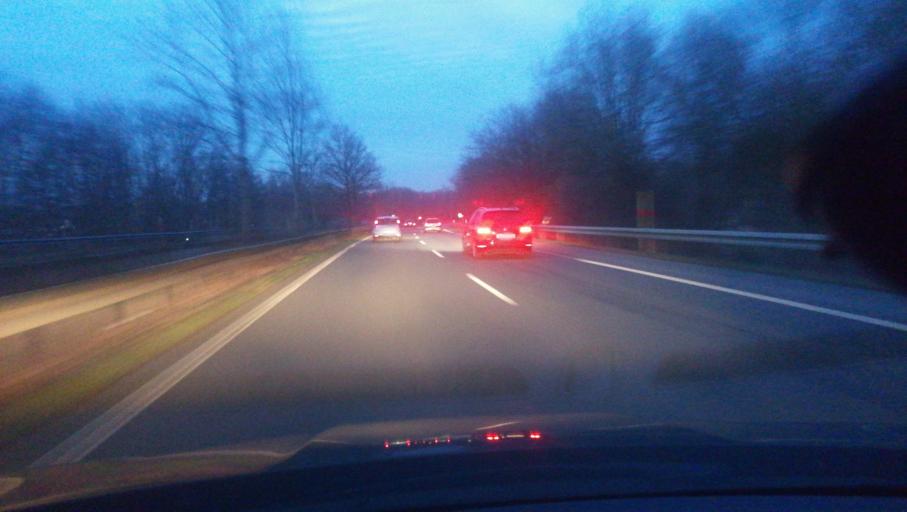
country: DE
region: North Rhine-Westphalia
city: Waltrop
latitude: 51.5524
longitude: 7.3995
